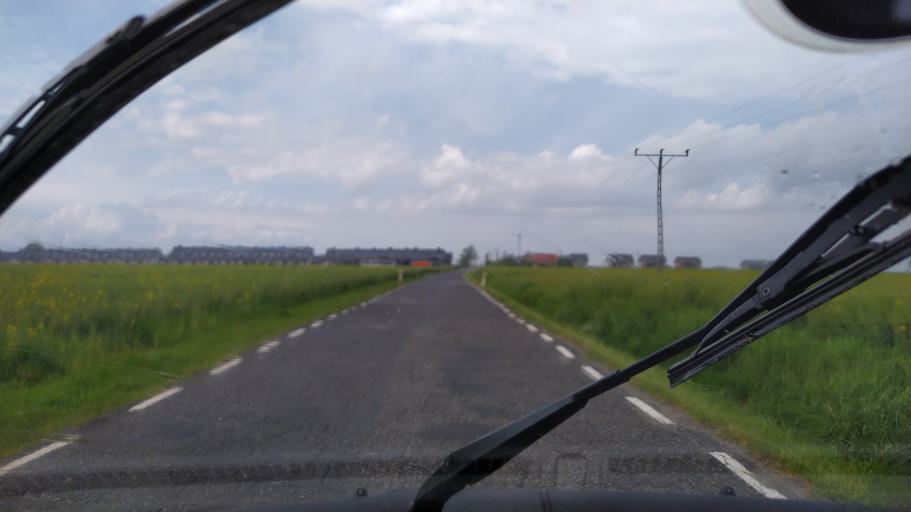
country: PL
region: Silesian Voivodeship
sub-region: Powiat gliwicki
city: Zernica
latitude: 50.2323
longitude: 18.6171
